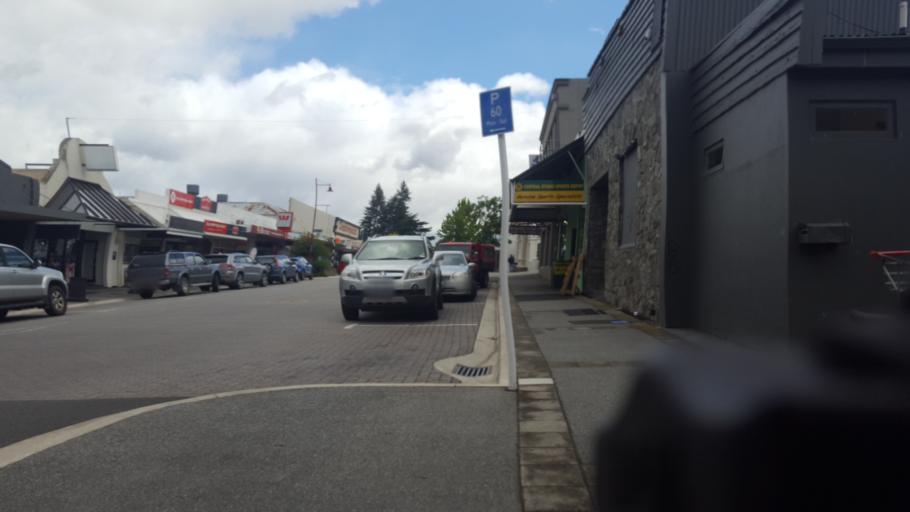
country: NZ
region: Otago
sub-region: Queenstown-Lakes District
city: Wanaka
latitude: -45.2576
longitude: 169.3931
